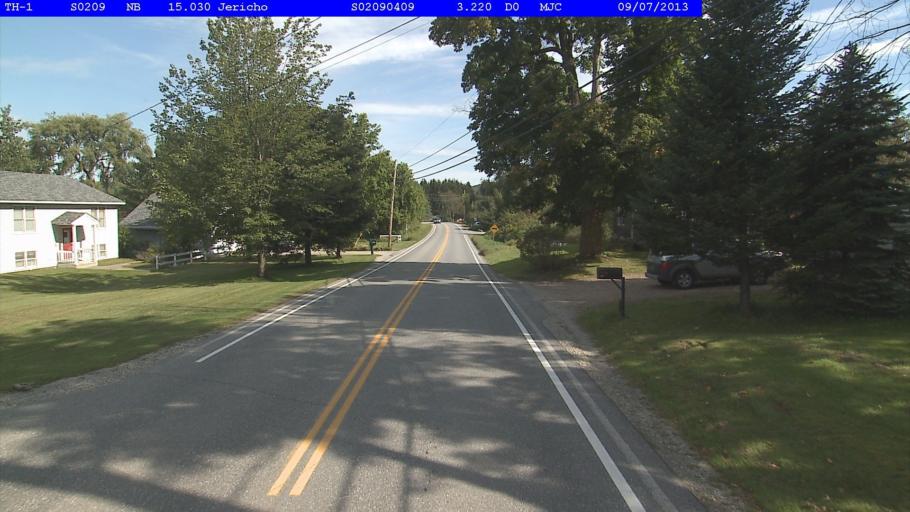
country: US
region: Vermont
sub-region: Chittenden County
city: Jericho
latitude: 44.4742
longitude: -72.9695
